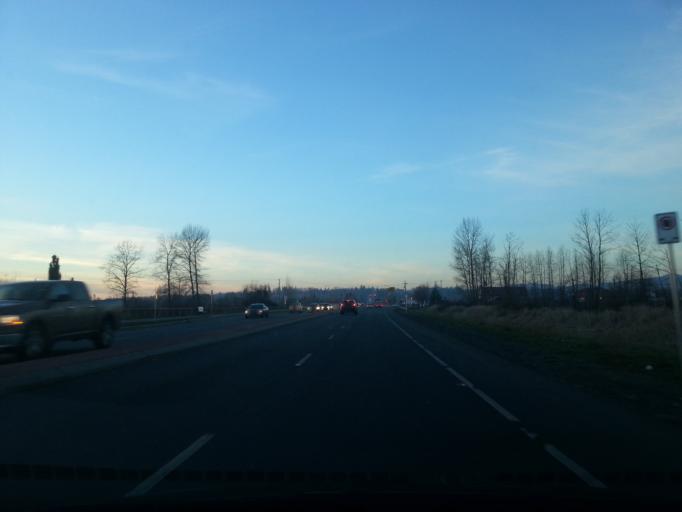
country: CA
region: British Columbia
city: Langley
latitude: 49.1366
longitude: -122.7311
